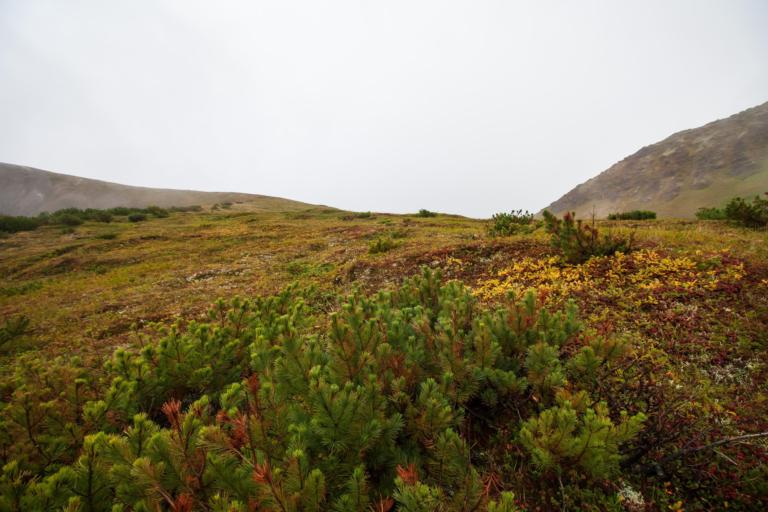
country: RU
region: Kamtsjatka
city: Yelizovo
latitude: 53.9759
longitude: 158.0833
